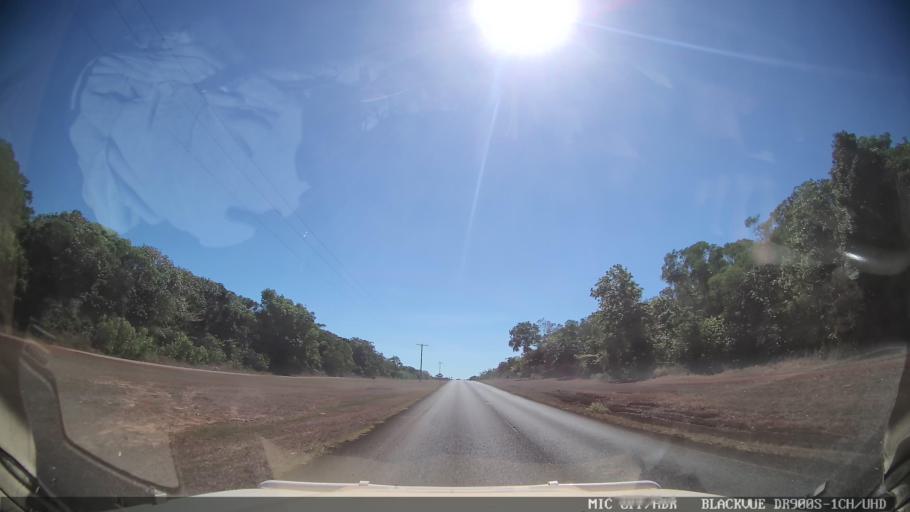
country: AU
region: Queensland
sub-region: Torres
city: Thursday Island
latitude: -10.9023
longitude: 142.3336
